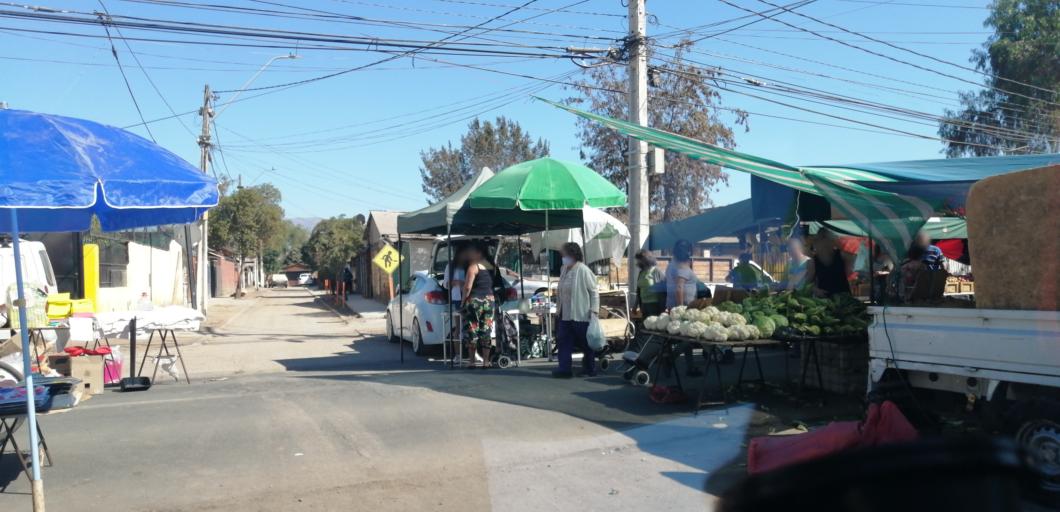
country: CL
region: Santiago Metropolitan
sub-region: Provincia de Santiago
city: Lo Prado
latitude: -33.4374
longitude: -70.7583
